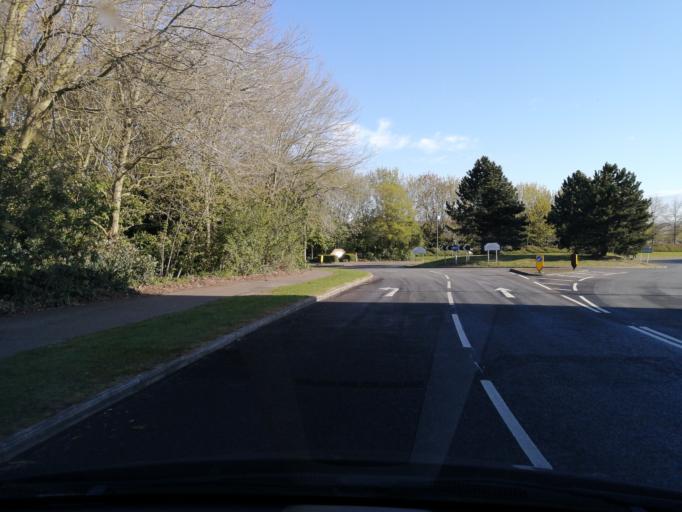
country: GB
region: England
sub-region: Peterborough
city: Castor
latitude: 52.5508
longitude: -0.3232
